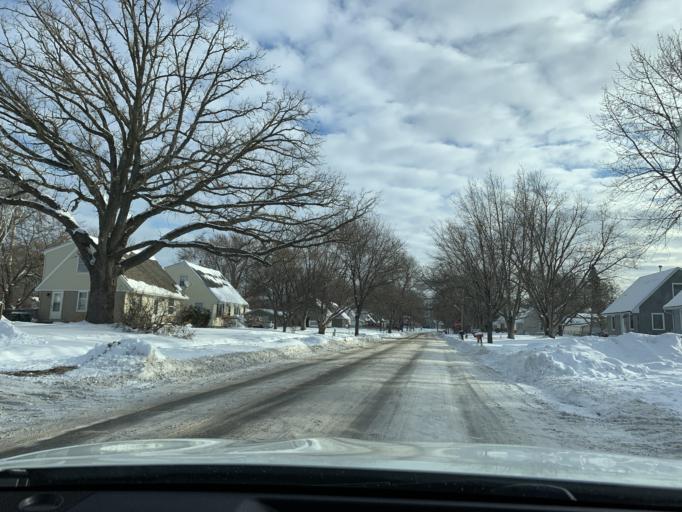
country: US
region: Minnesota
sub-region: Anoka County
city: Coon Rapids
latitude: 45.1679
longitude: -93.2828
